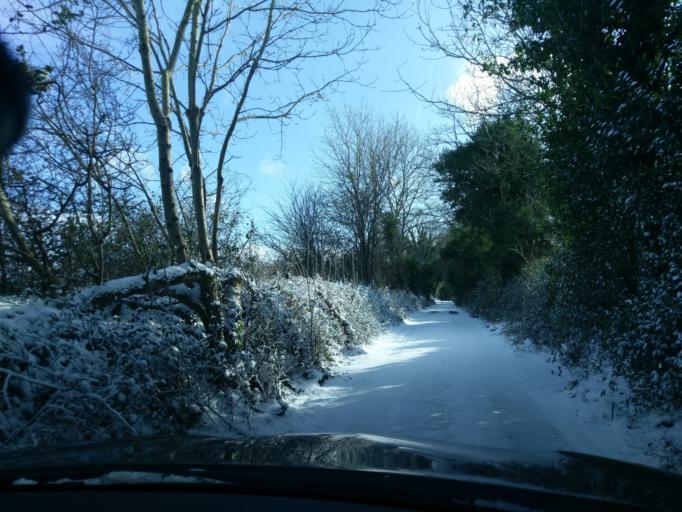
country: IE
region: Connaught
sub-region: County Galway
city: Athenry
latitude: 53.2101
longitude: -8.7695
